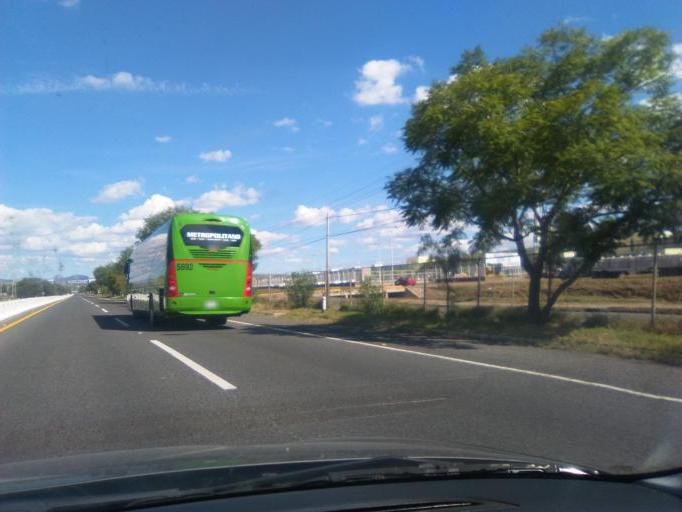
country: MX
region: Guanajuato
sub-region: Silao de la Victoria
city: Aguas Buenas
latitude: 20.9505
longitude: -101.3919
